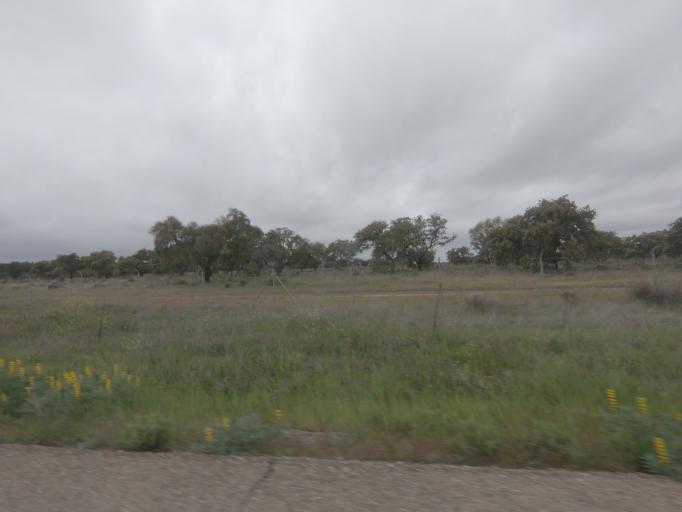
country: ES
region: Extremadura
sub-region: Provincia de Badajoz
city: Villar del Rey
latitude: 38.9896
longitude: -6.8759
